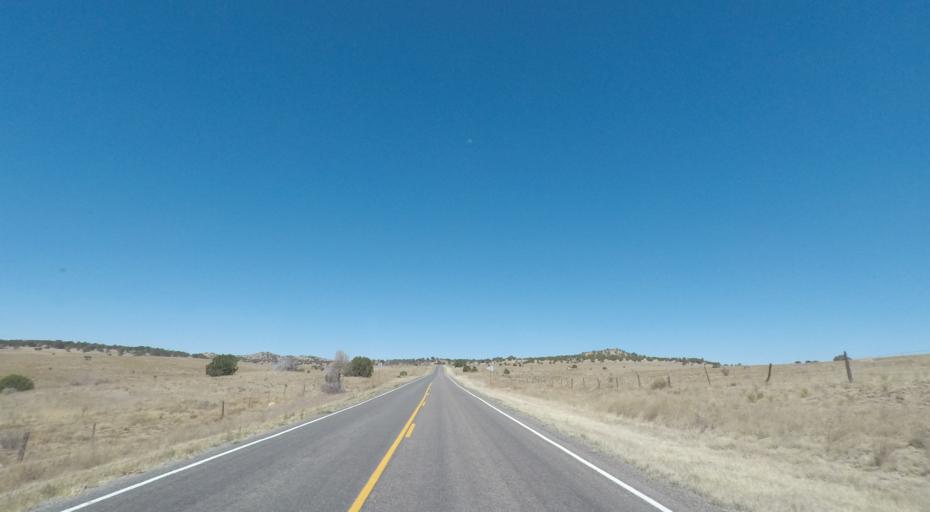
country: US
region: New Mexico
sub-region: Lincoln County
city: Capitan
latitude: 33.5214
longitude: -105.4979
